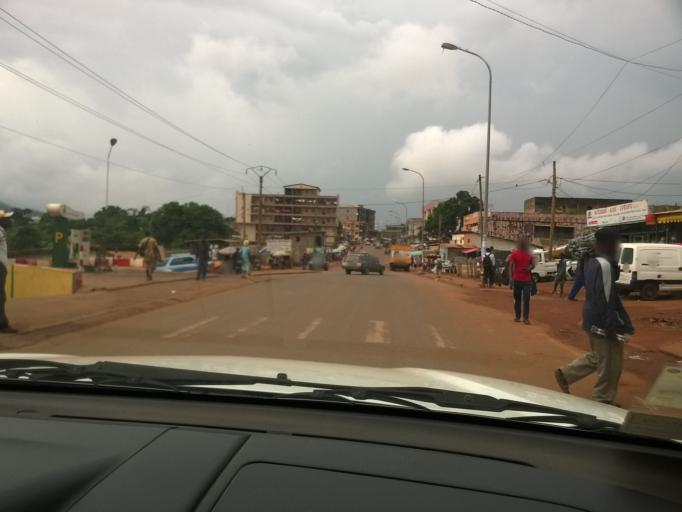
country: CM
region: Centre
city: Yaounde
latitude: 3.9098
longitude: 11.5249
